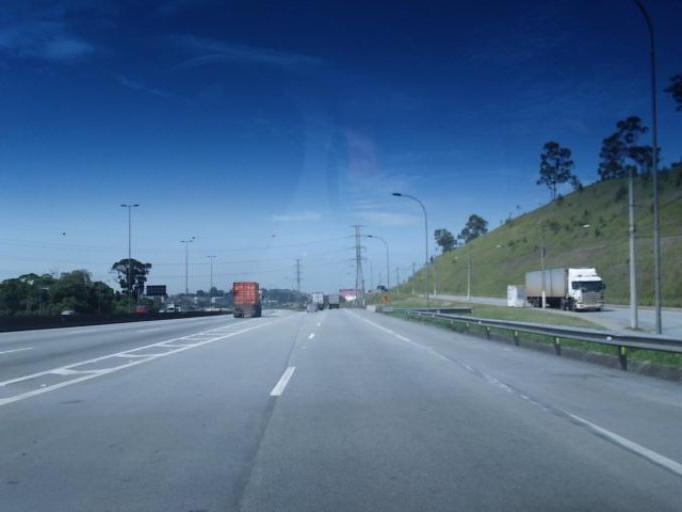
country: BR
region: Sao Paulo
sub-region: Embu
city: Embu
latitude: -23.6338
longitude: -46.8331
